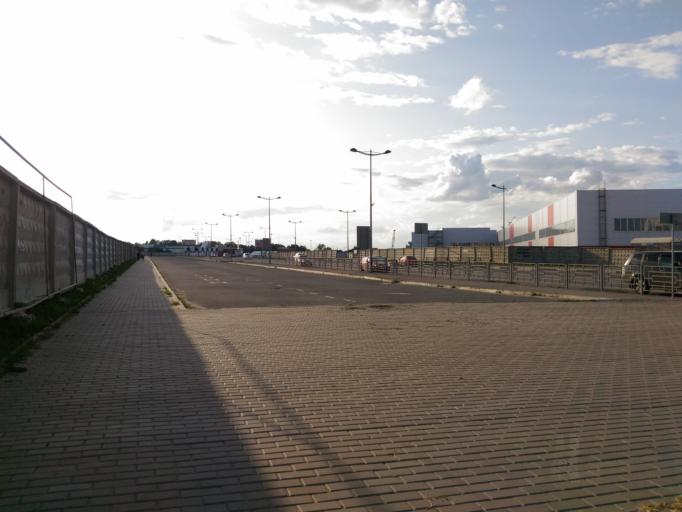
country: RU
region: Ulyanovsk
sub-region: Ulyanovskiy Rayon
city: Ulyanovsk
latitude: 54.2878
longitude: 48.2770
